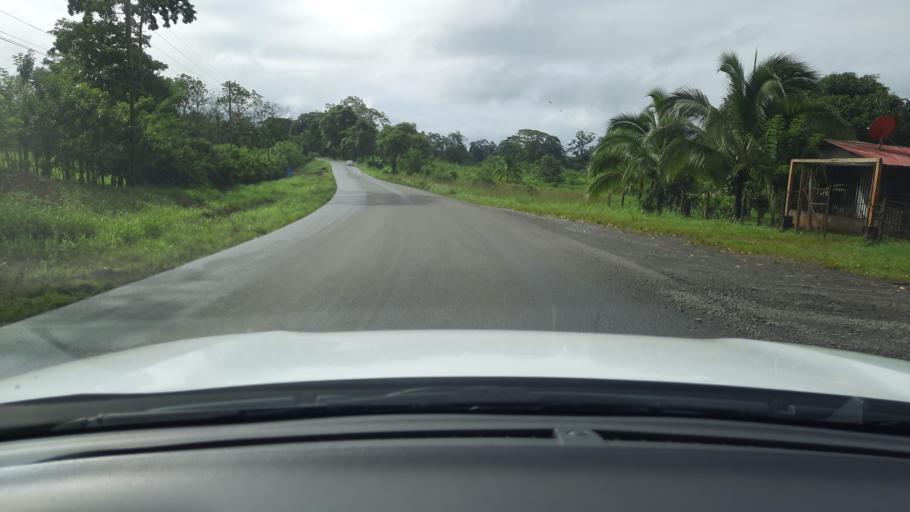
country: CR
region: Alajuela
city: San Jose
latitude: 10.9360
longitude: -85.1082
